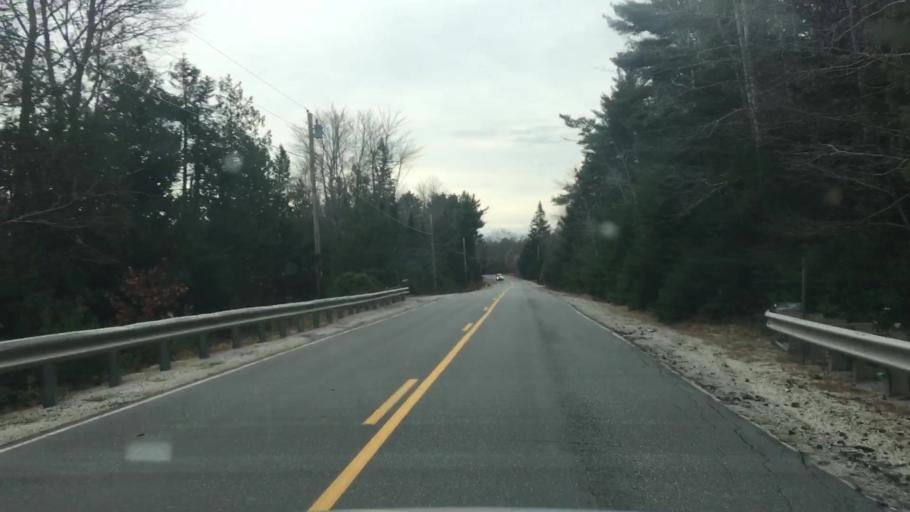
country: US
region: Maine
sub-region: Hancock County
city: Penobscot
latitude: 44.4256
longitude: -68.6239
